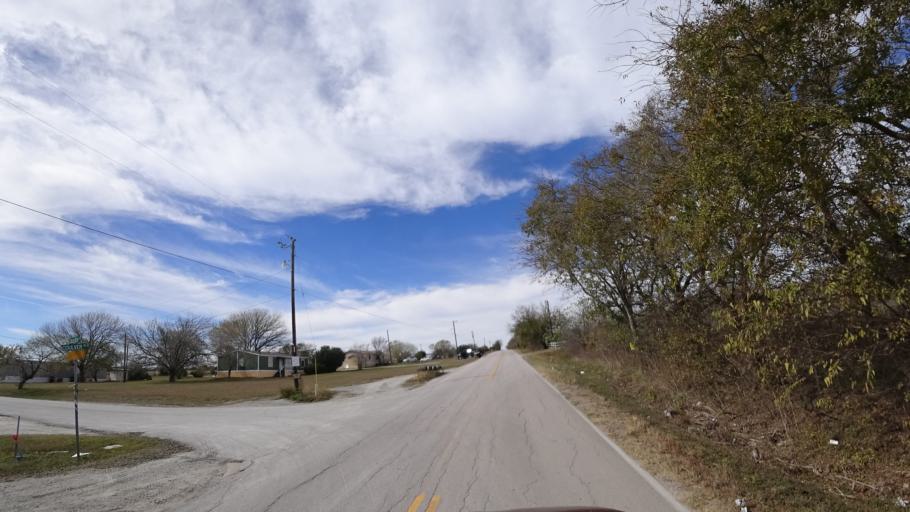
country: US
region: Texas
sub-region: Travis County
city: Onion Creek
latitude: 30.1178
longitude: -97.7274
